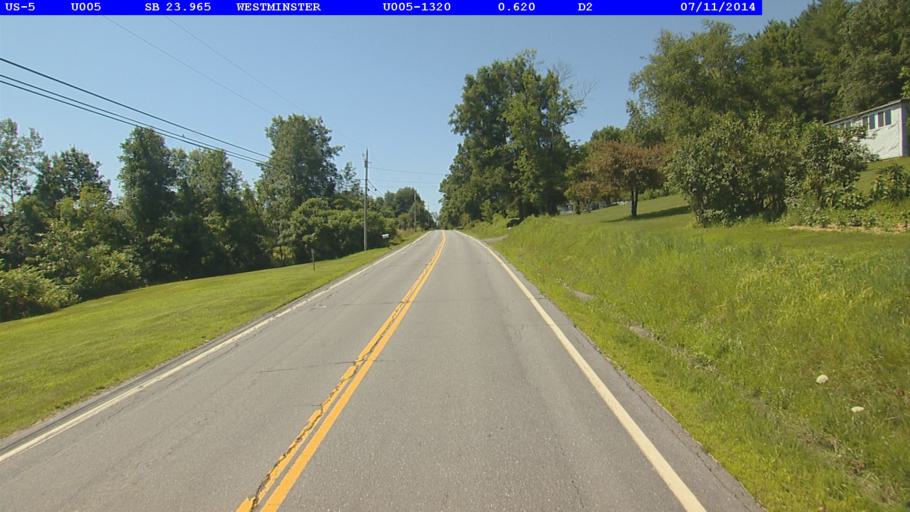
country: US
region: New Hampshire
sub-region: Cheshire County
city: Westmoreland
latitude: 43.0292
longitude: -72.4680
